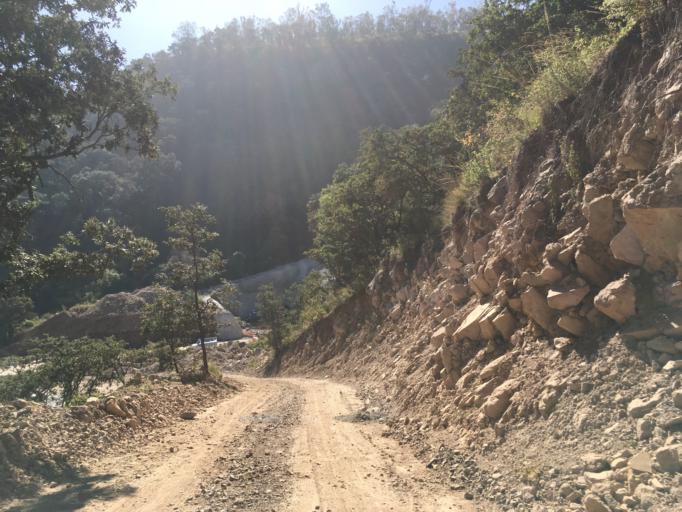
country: MX
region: Michoacan
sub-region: Morelia
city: Montana Monarca (Punta Altozano)
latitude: 19.6720
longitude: -101.1512
